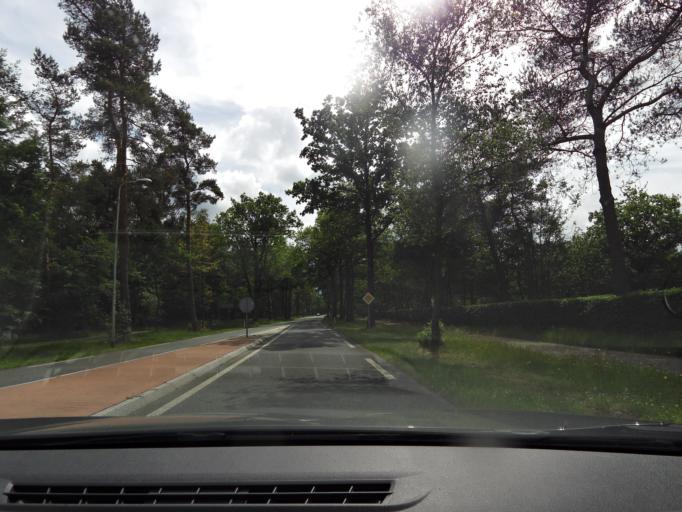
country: NL
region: Gelderland
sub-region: Gemeente Barneveld
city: Garderen
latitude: 52.2197
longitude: 5.7080
